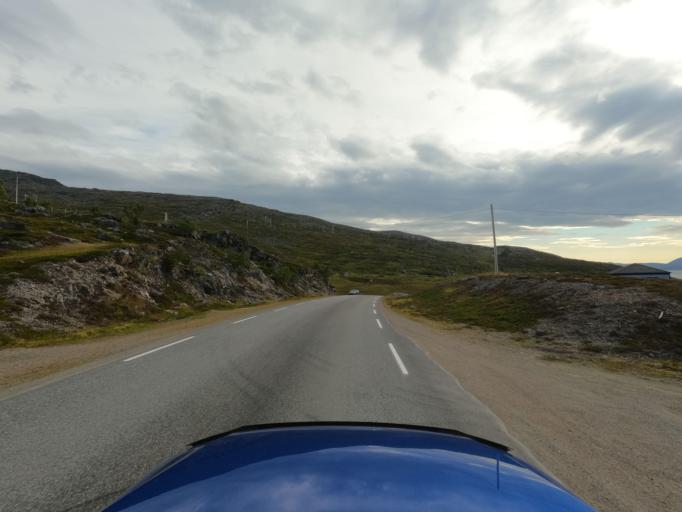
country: NO
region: Finnmark Fylke
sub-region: Hammerfest
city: Rypefjord
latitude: 70.6020
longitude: 23.6868
